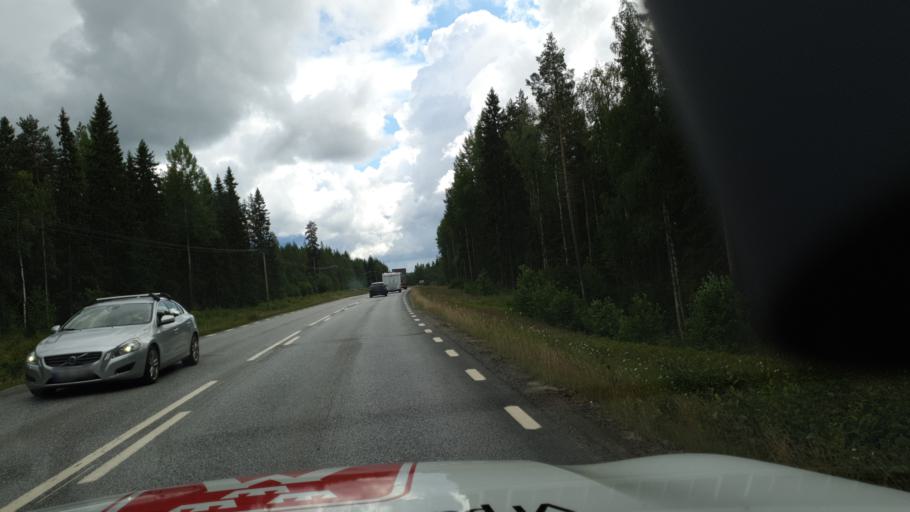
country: SE
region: Vaesterbotten
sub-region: Vannas Kommun
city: Vaennaes
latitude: 63.9388
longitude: 19.7716
